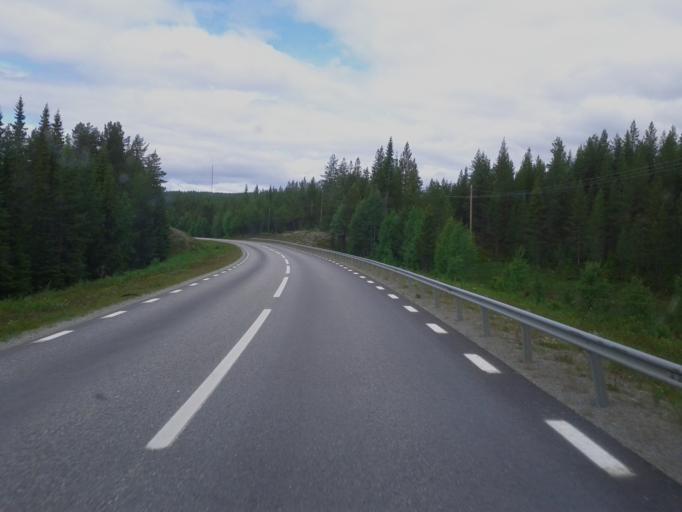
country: SE
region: Vaesterbotten
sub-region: Storumans Kommun
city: Fristad
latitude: 65.3809
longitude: 16.5119
